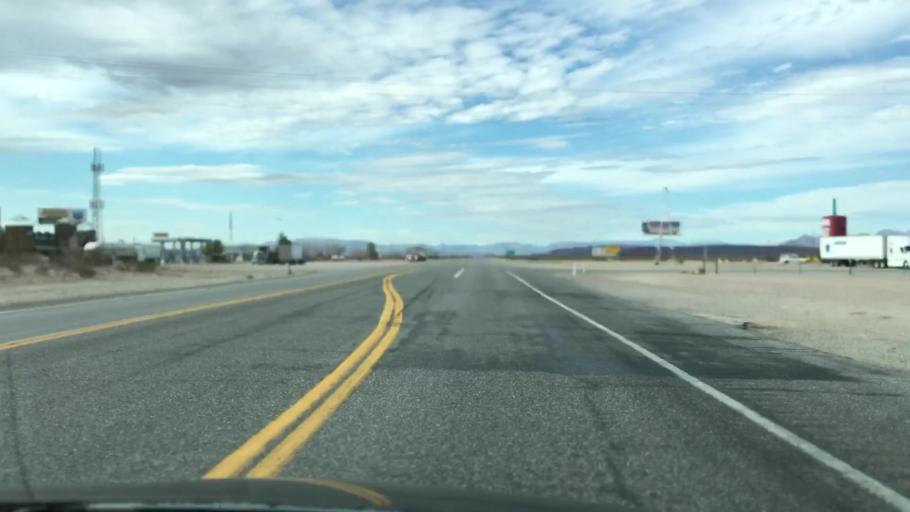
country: US
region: Nevada
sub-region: Nye County
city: Beatty
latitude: 36.6426
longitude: -116.3955
